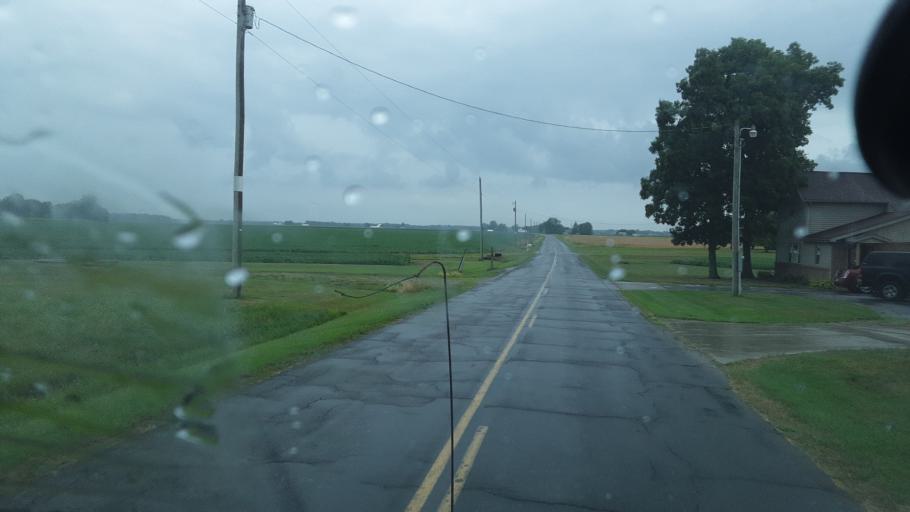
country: US
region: Ohio
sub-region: Williams County
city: Edgerton
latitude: 41.4979
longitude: -84.7984
